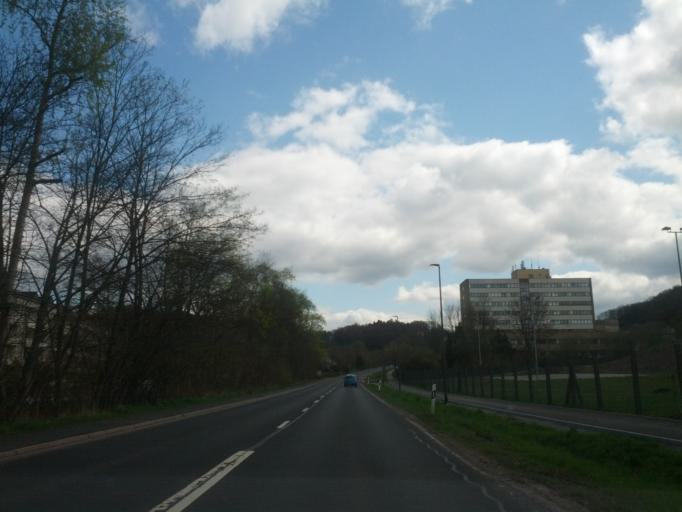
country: DE
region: Thuringia
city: Seebach
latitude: 50.9110
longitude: 10.4270
